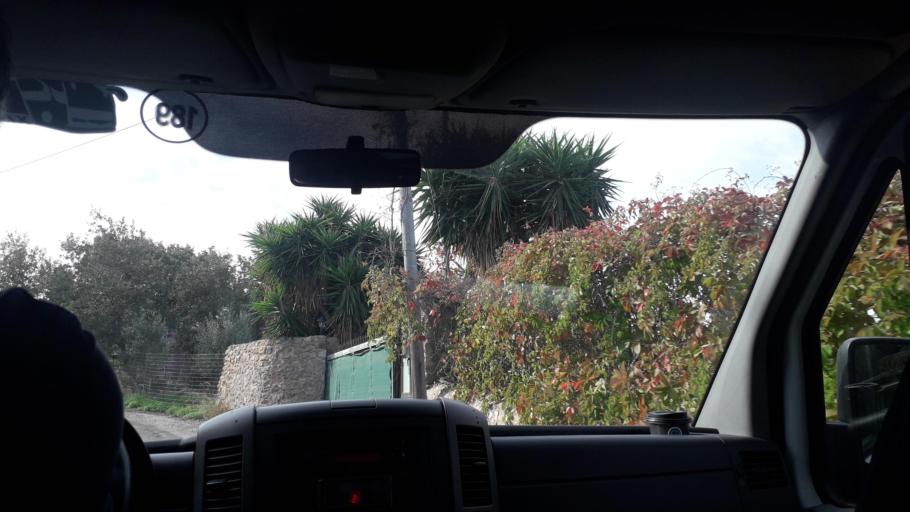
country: GR
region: Crete
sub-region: Nomos Rethymnis
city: Atsipopoulon
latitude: 35.3622
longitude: 24.4341
